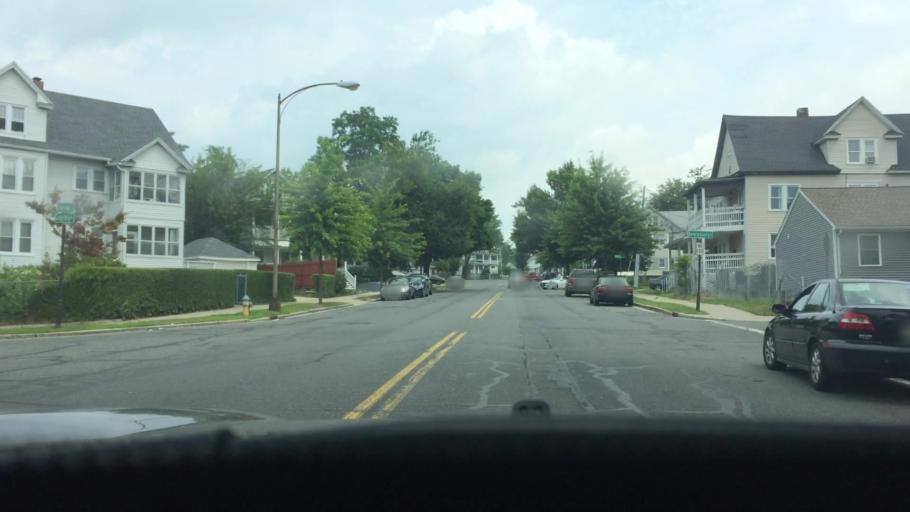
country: US
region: Massachusetts
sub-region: Hampden County
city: Springfield
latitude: 42.1174
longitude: -72.5950
